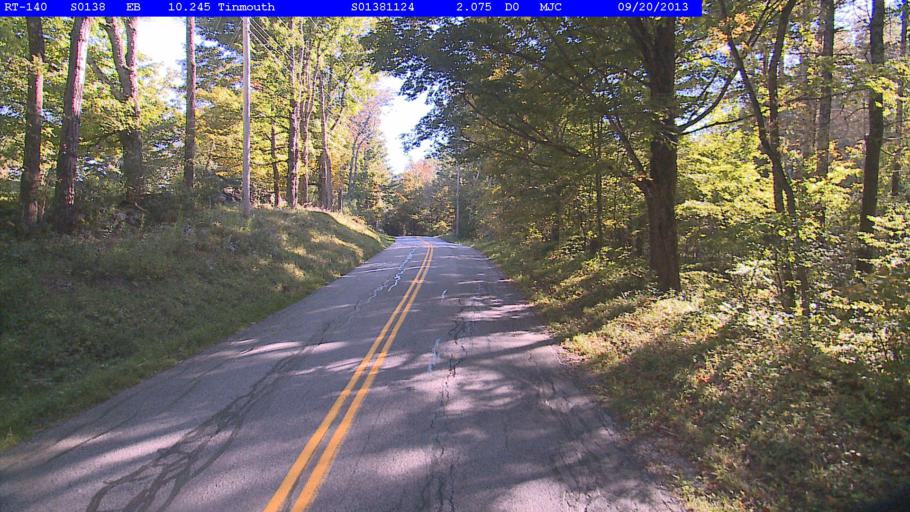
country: US
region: Vermont
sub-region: Rutland County
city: West Rutland
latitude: 43.4655
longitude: -73.0474
